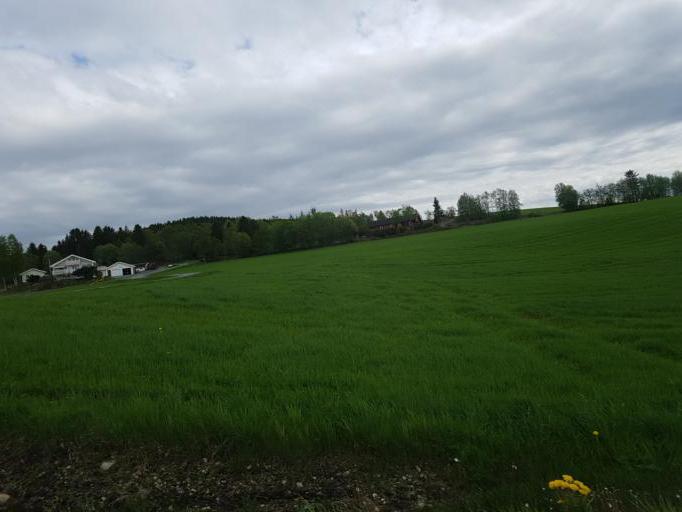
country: NO
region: Nord-Trondelag
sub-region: Levanger
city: Skogn
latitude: 63.7073
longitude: 11.2443
